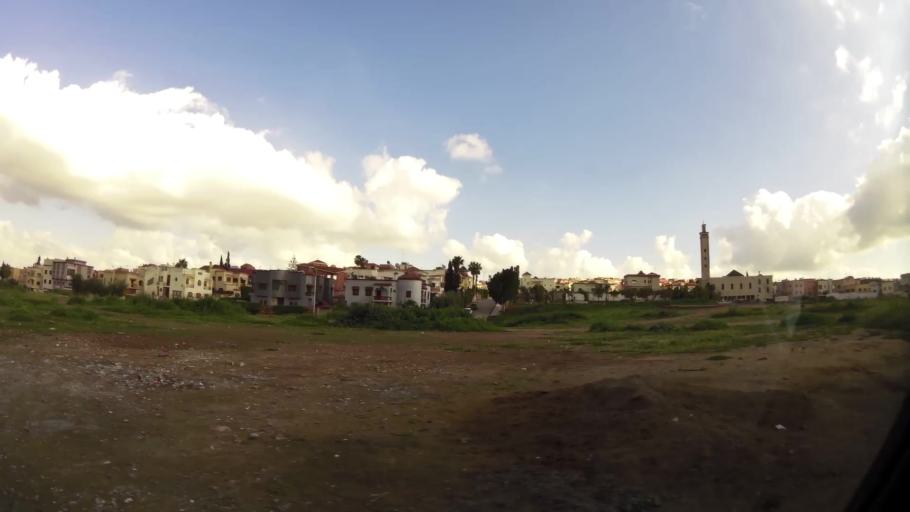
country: MA
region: Chaouia-Ouardigha
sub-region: Settat Province
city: Settat
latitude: 33.0117
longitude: -7.6310
